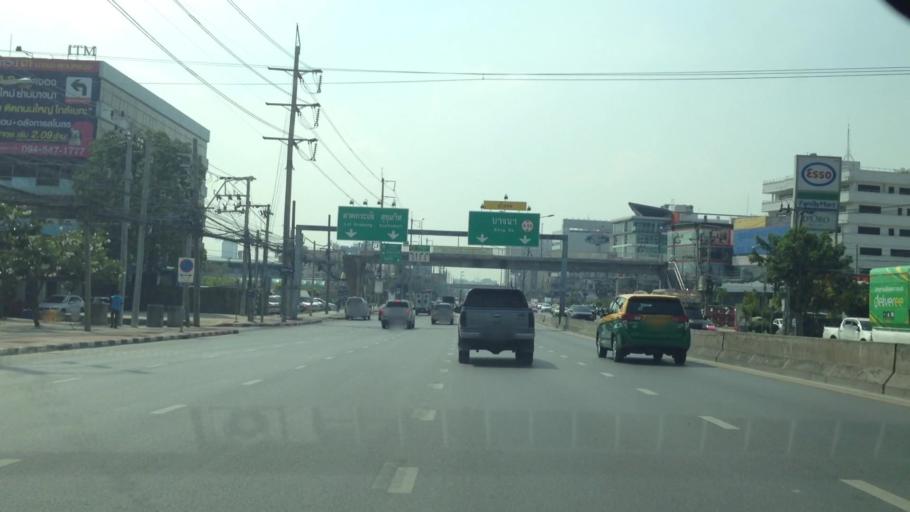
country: TH
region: Bangkok
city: Bang Na
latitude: 13.6827
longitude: 100.6465
